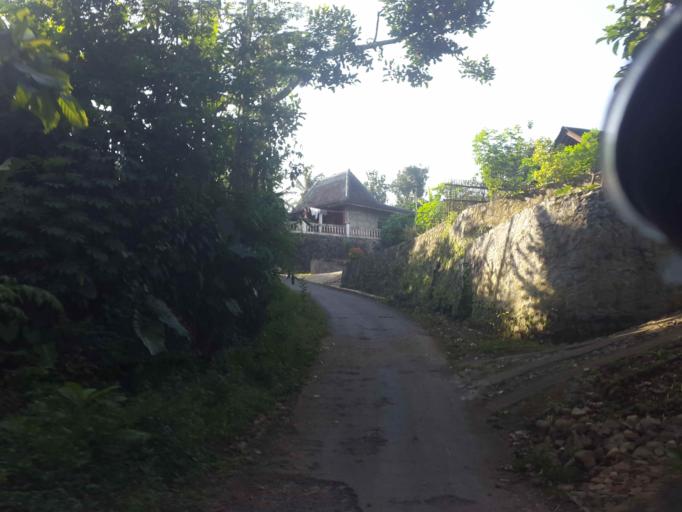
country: ID
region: Central Java
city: Jatiroto
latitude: -7.7895
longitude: 111.1054
